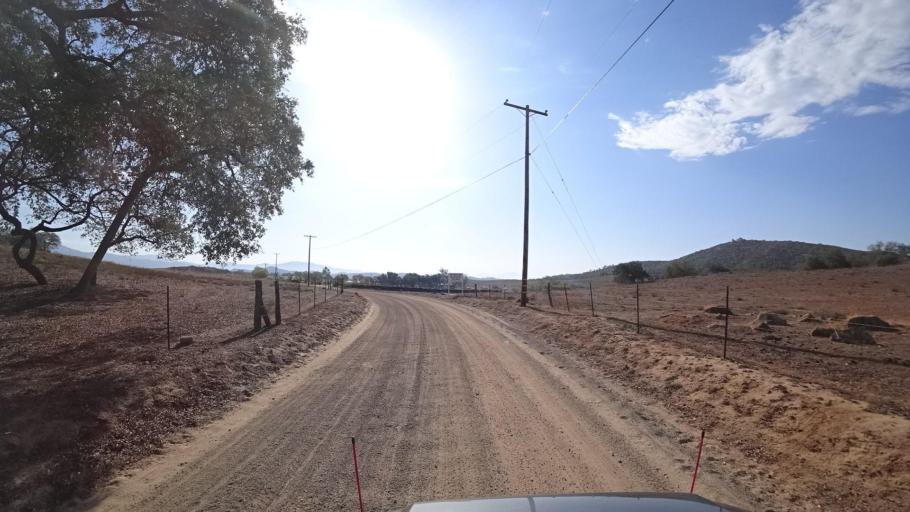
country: US
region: California
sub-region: San Diego County
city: San Pasqual
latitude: 33.1668
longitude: -116.9566
